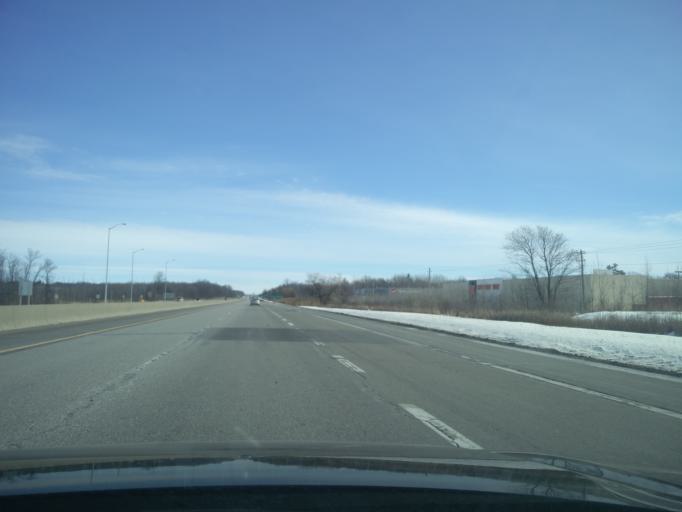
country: CA
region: Ontario
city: Prescott
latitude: 44.7236
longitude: -75.5239
